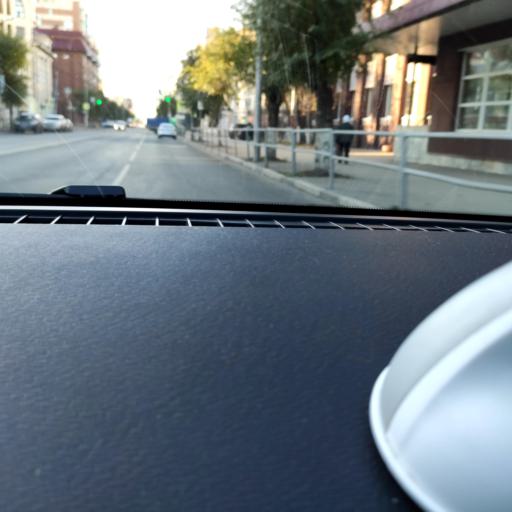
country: RU
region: Samara
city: Samara
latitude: 53.1975
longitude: 50.1085
